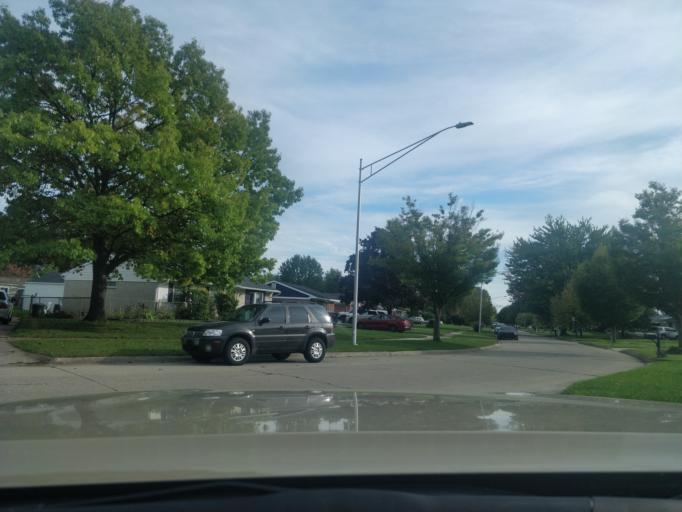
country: US
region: Michigan
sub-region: Wayne County
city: Belleville
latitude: 42.2261
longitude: -83.4534
